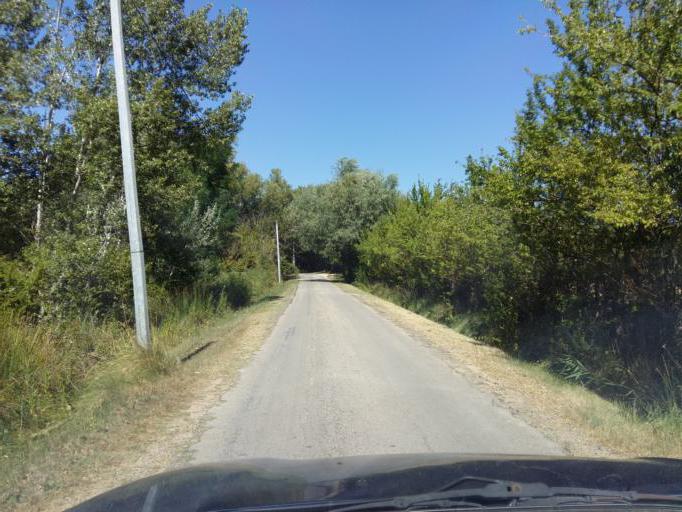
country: FR
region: Provence-Alpes-Cote d'Azur
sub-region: Departement du Vaucluse
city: Loriol-du-Comtat
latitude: 44.0869
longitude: 5.0109
